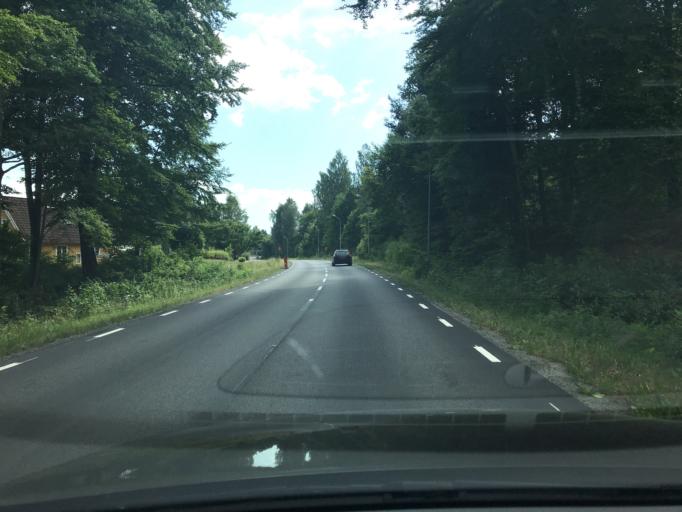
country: SE
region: Skane
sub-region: Hassleholms Kommun
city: Hastveda
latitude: 56.2864
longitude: 13.9161
